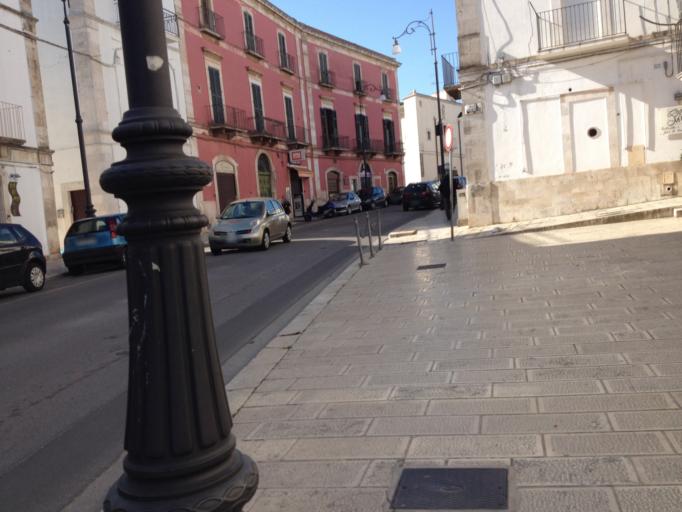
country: IT
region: Apulia
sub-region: Provincia di Bari
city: Putignano
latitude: 40.8493
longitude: 17.1253
